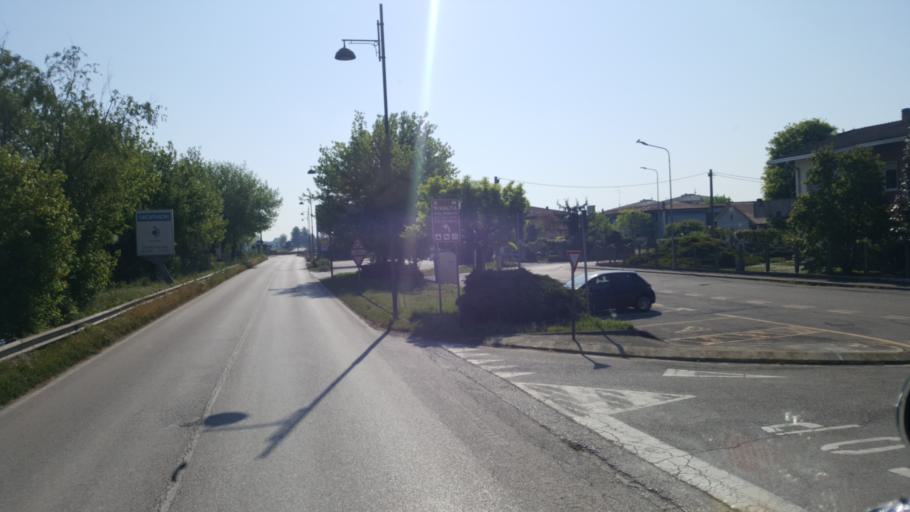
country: IT
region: Lombardy
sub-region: Provincia di Mantova
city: Castellucchio
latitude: 45.1540
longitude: 10.6532
